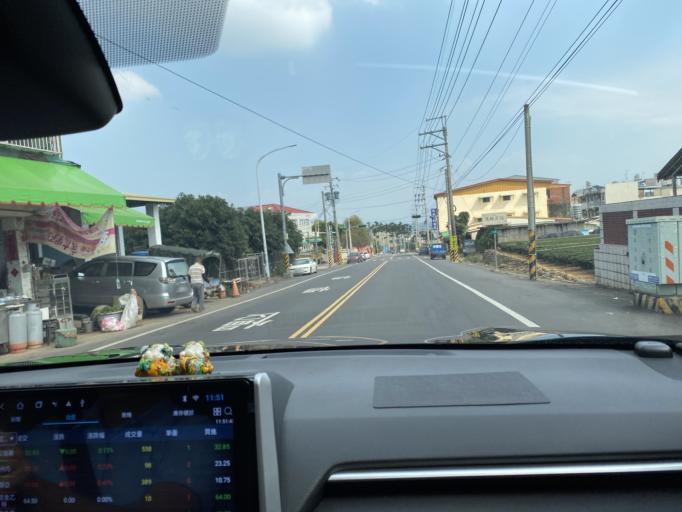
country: TW
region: Taiwan
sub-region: Nantou
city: Nantou
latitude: 23.8354
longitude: 120.6611
